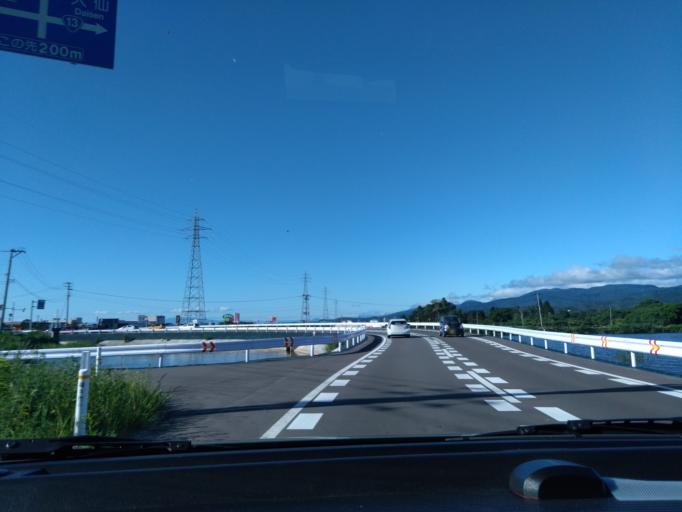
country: JP
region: Akita
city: Yokotemachi
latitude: 39.2899
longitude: 140.5537
